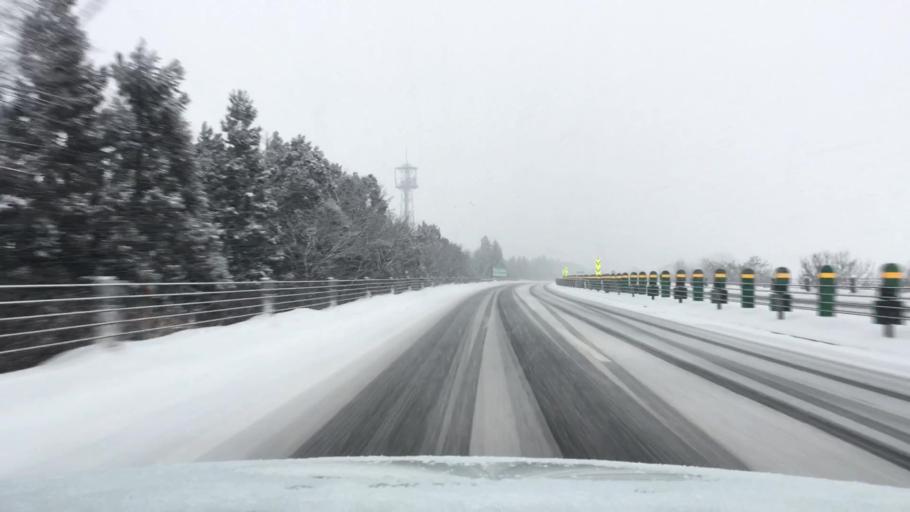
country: JP
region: Akita
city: Hanawa
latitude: 40.2205
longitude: 140.7914
